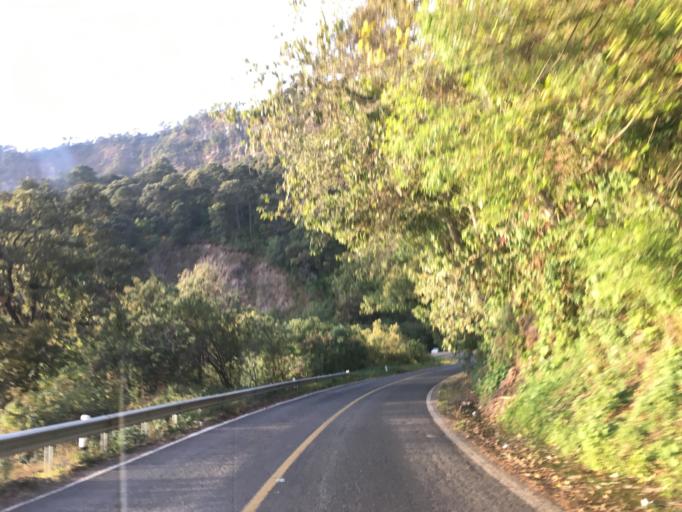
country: MX
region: Michoacan
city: Tzitzio
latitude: 19.6523
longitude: -100.9490
